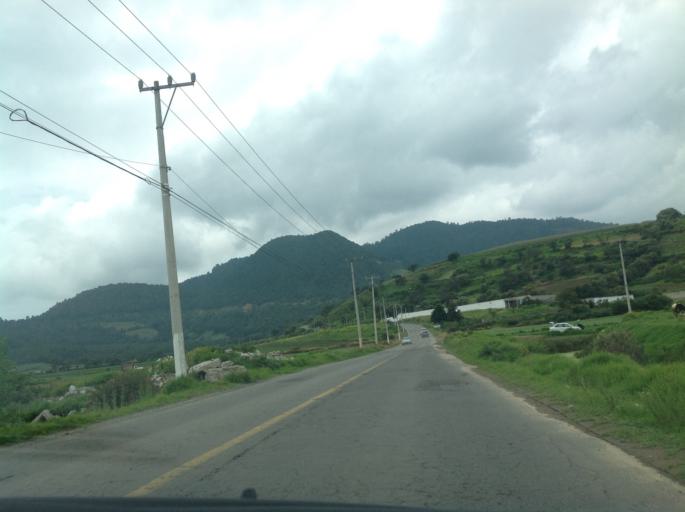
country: MX
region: Mexico
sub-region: Tenango del Valle
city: Santa Maria Jajalpa
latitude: 19.1087
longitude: -99.5309
